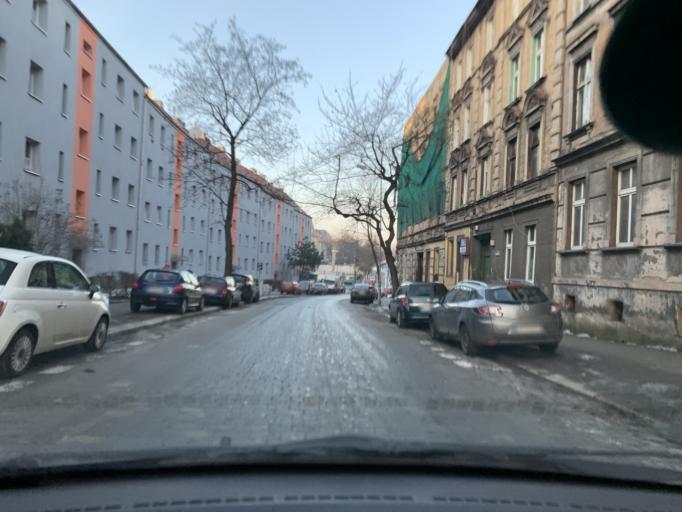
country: PL
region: Silesian Voivodeship
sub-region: Bytom
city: Bytom
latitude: 50.3499
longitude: 18.9158
